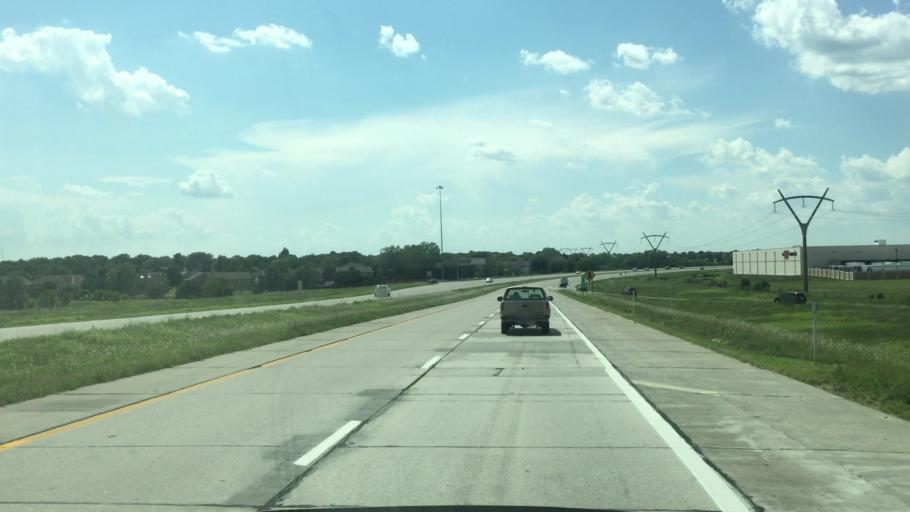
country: US
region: Kansas
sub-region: Sedgwick County
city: Bellaire
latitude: 37.7300
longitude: -97.2103
